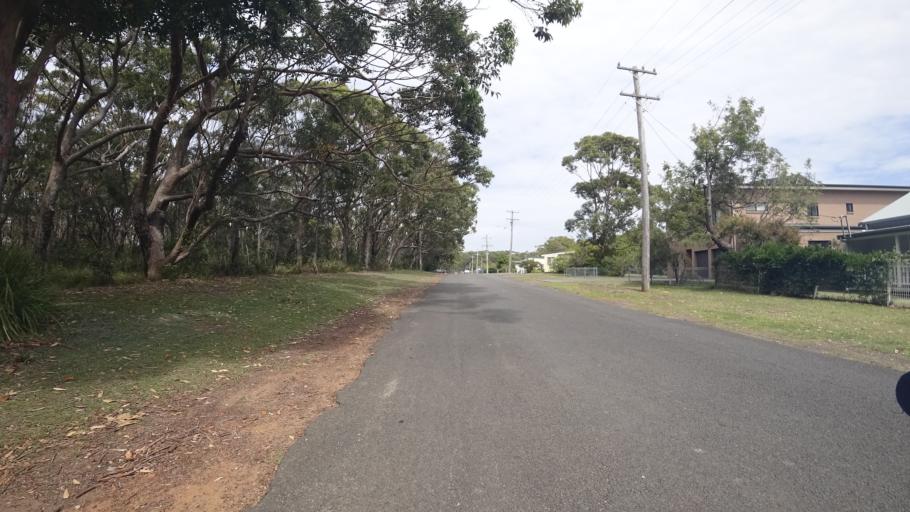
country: AU
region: New South Wales
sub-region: Shoalhaven Shire
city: Milton
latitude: -35.2468
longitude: 150.5336
